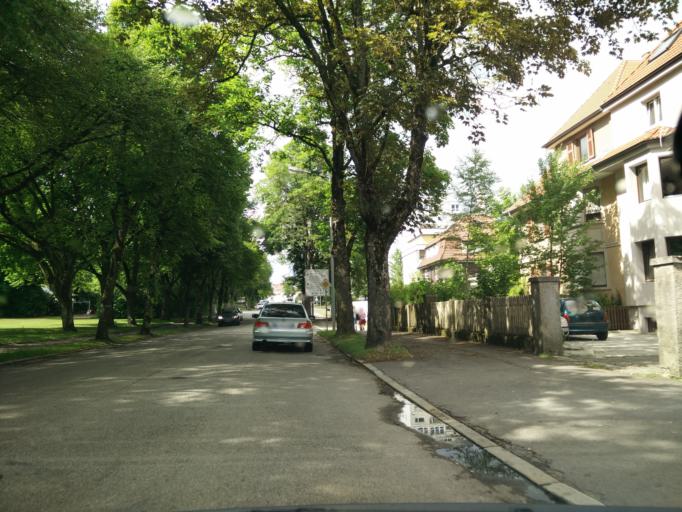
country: DE
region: Baden-Wuerttemberg
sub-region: Freiburg Region
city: Villingen-Schwenningen
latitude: 48.0555
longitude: 8.5274
